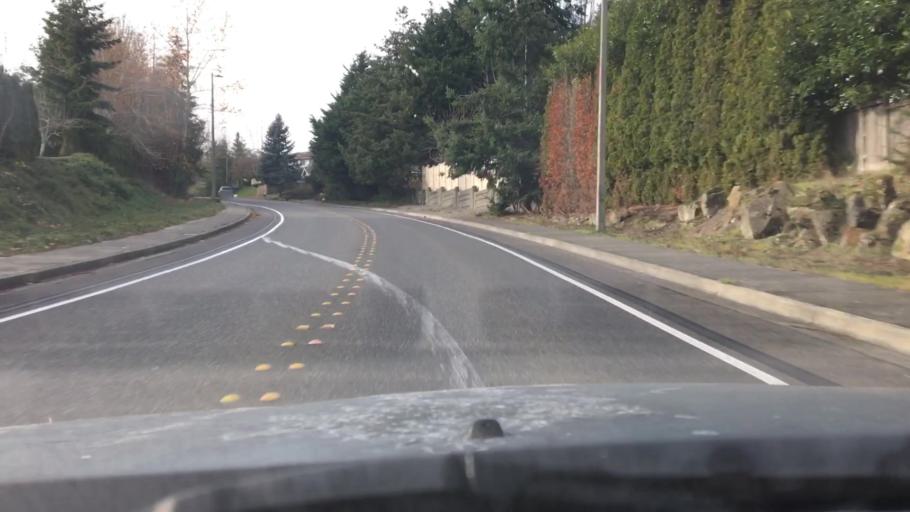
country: US
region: Washington
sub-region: Whatcom County
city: Geneva
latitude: 48.7727
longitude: -122.4120
